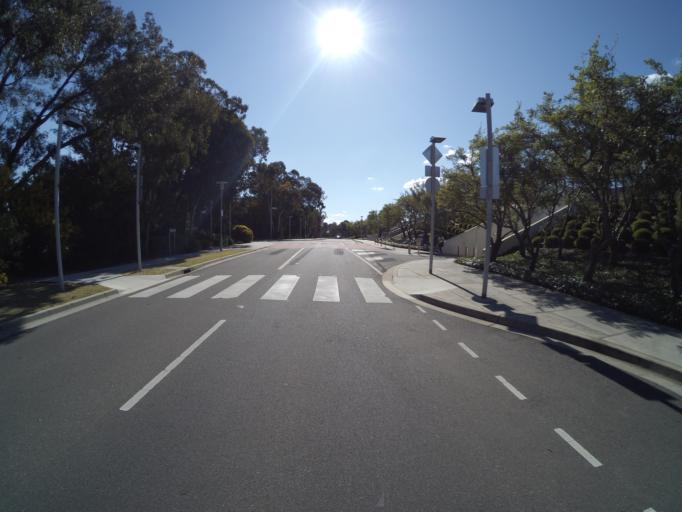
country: AU
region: Australian Capital Territory
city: Forrest
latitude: -35.3102
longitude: 149.1233
